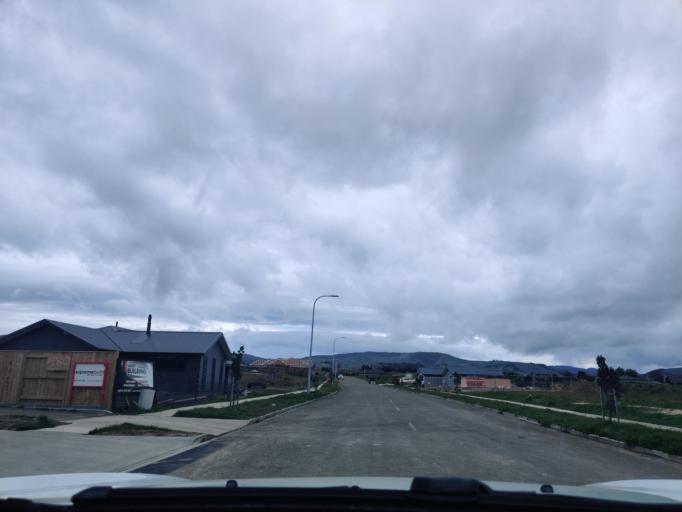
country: NZ
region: Manawatu-Wanganui
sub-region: Palmerston North City
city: Palmerston North
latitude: -40.3880
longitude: 175.6472
